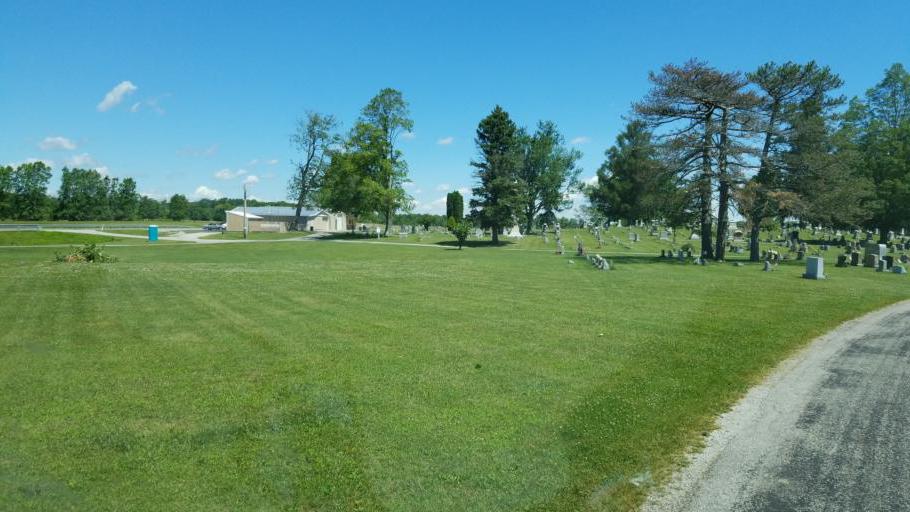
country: US
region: Ohio
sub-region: Morrow County
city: Cardington
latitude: 40.6322
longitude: -82.9588
